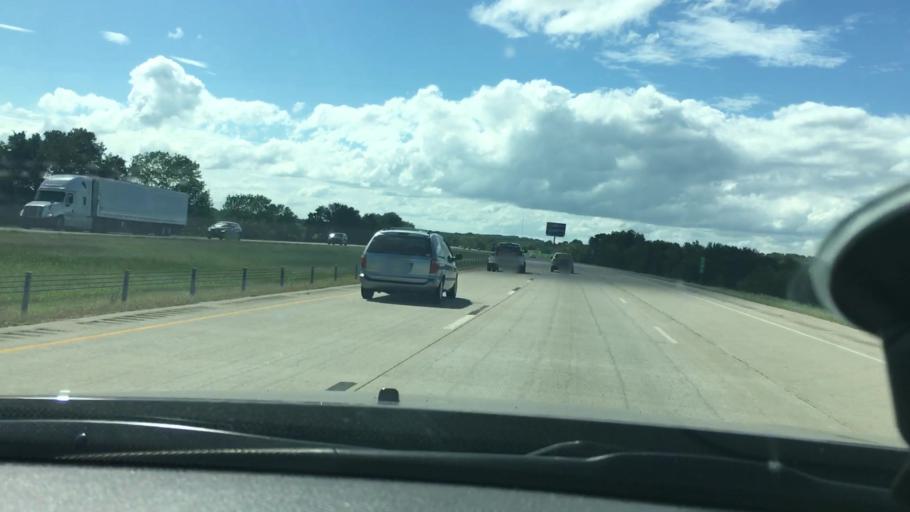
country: US
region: Oklahoma
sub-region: Muskogee County
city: Warner
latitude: 35.4879
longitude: -95.1737
